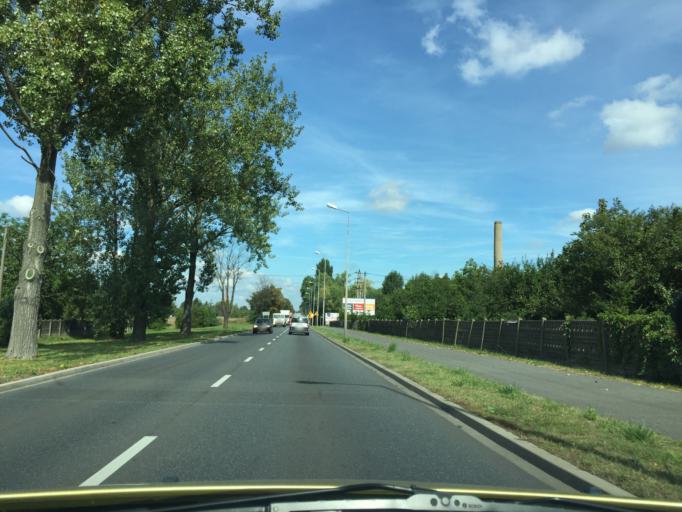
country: PL
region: Greater Poland Voivodeship
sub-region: Kalisz
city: Kalisz
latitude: 51.7899
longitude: 18.0907
